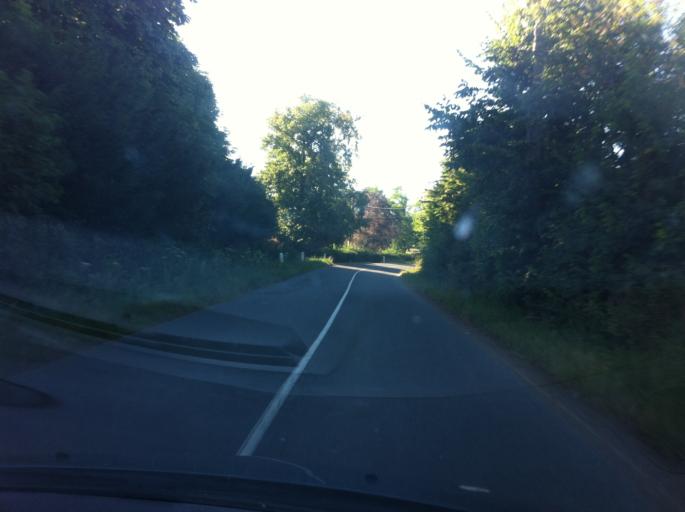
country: FR
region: Auvergne
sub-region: Departement de l'Allier
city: Chantelle
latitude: 46.2740
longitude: 3.1183
